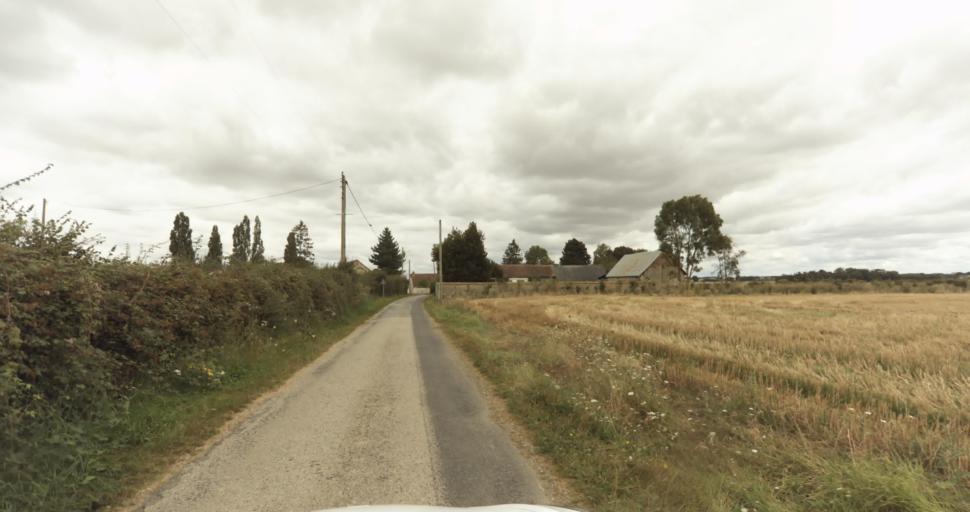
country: FR
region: Haute-Normandie
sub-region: Departement de l'Eure
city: Nonancourt
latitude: 48.7955
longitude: 1.1325
